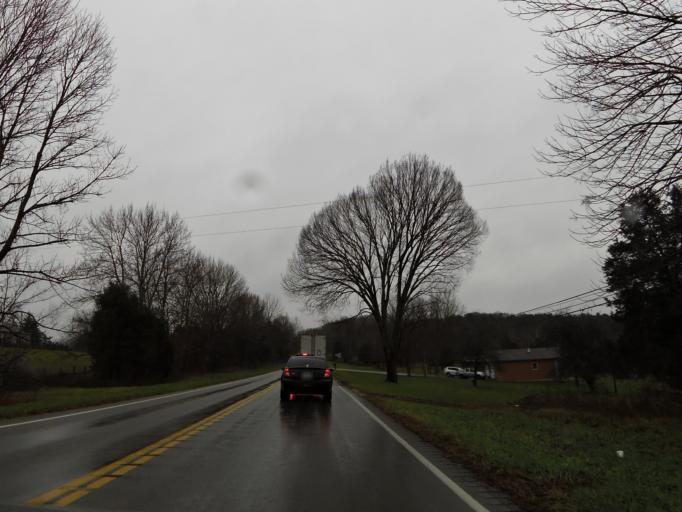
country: US
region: Kentucky
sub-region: Rockcastle County
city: Mount Vernon
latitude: 37.4244
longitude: -84.3332
